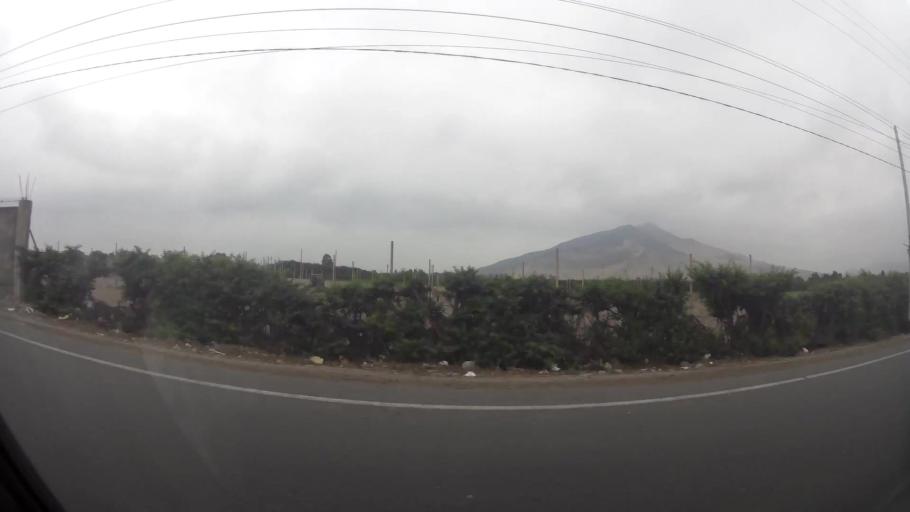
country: PE
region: Lima
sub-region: Provincia de Huaral
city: Huaral
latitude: -11.5127
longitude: -77.2336
